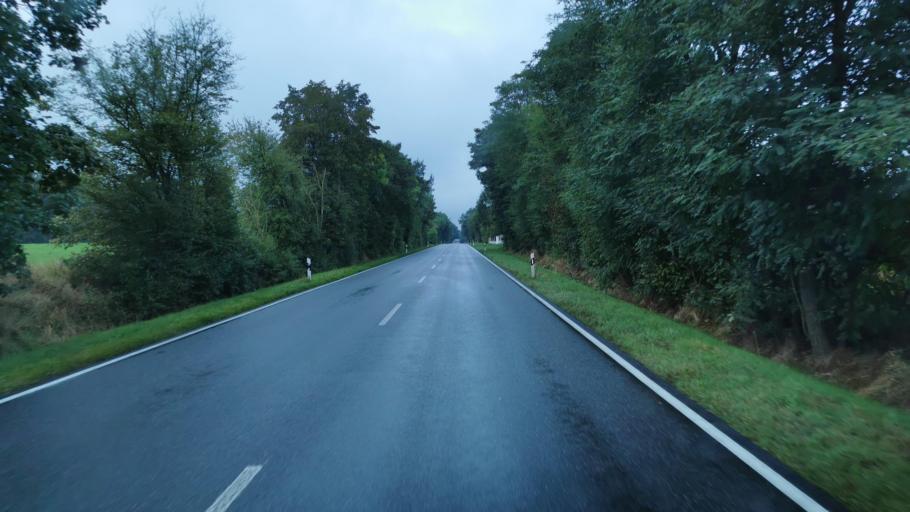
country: DE
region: North Rhine-Westphalia
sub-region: Regierungsbezirk Munster
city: Vreden
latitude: 52.1067
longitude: 6.8930
